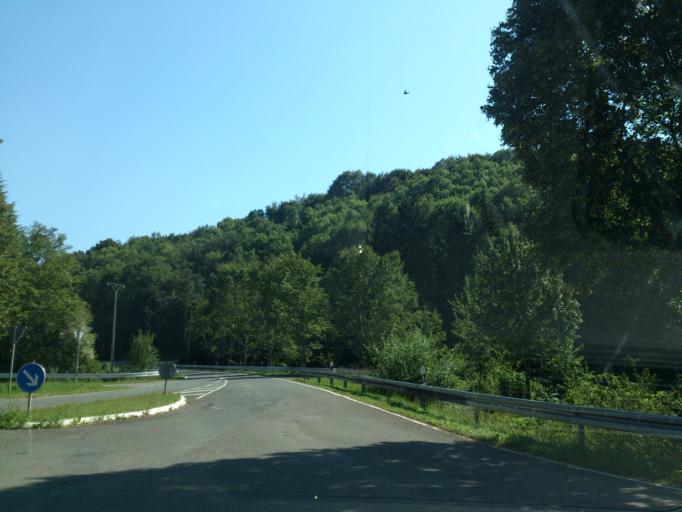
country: DE
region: North Rhine-Westphalia
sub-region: Regierungsbezirk Detmold
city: Willebadessen
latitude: 51.6273
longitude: 9.0443
